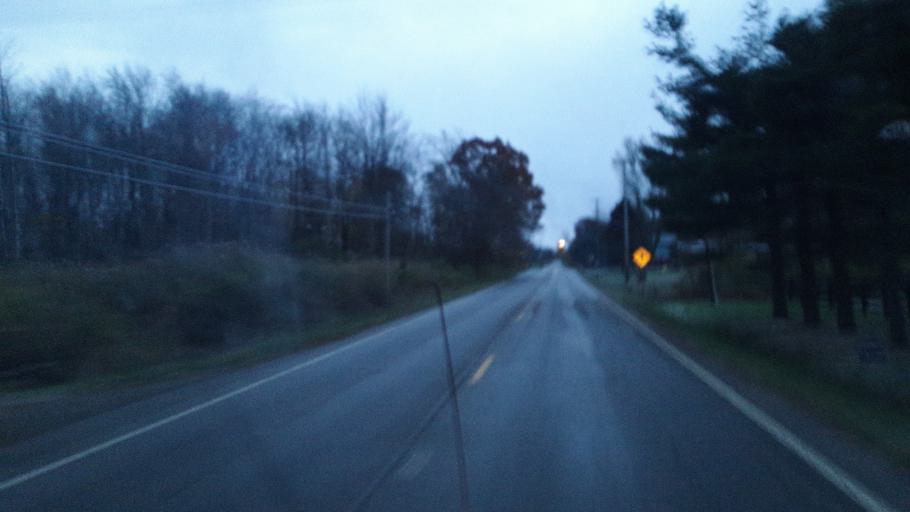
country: US
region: Ohio
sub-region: Portage County
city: Mantua
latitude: 41.3338
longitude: -81.2215
